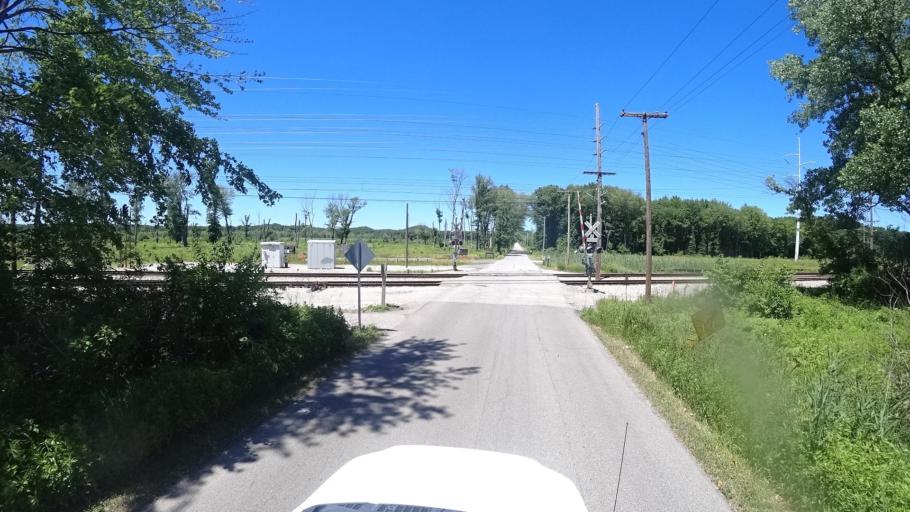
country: US
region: Indiana
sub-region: Porter County
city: Porter
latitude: 41.6363
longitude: -87.0867
